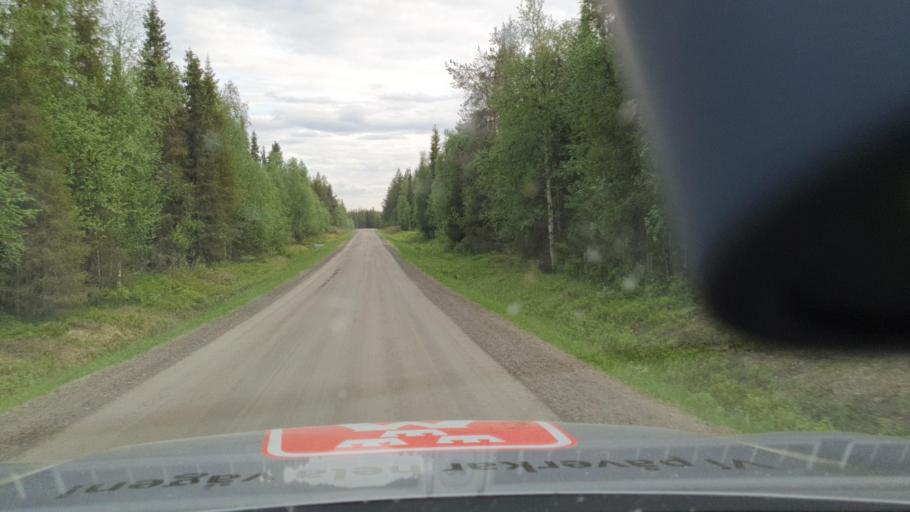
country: SE
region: Norrbotten
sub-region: Gallivare Kommun
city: Gaellivare
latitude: 66.6986
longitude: 21.1658
